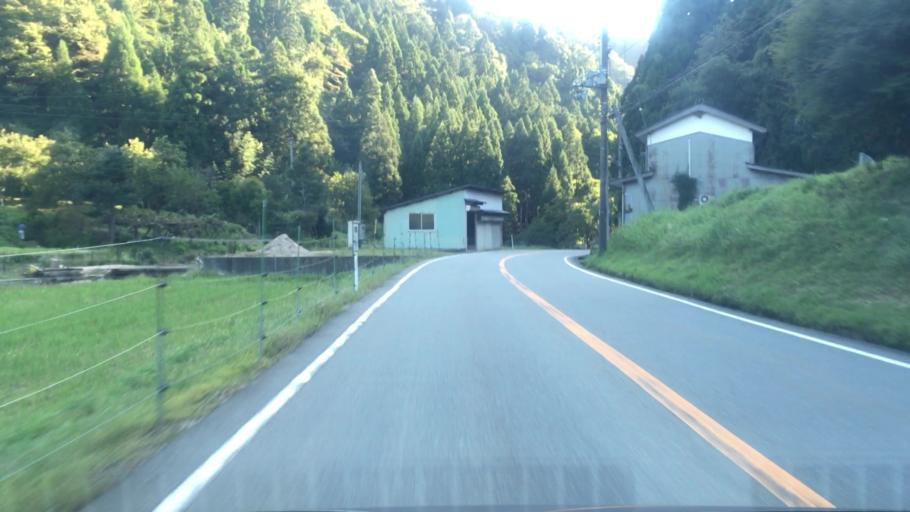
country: JP
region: Hyogo
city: Toyooka
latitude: 35.6202
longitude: 134.8618
